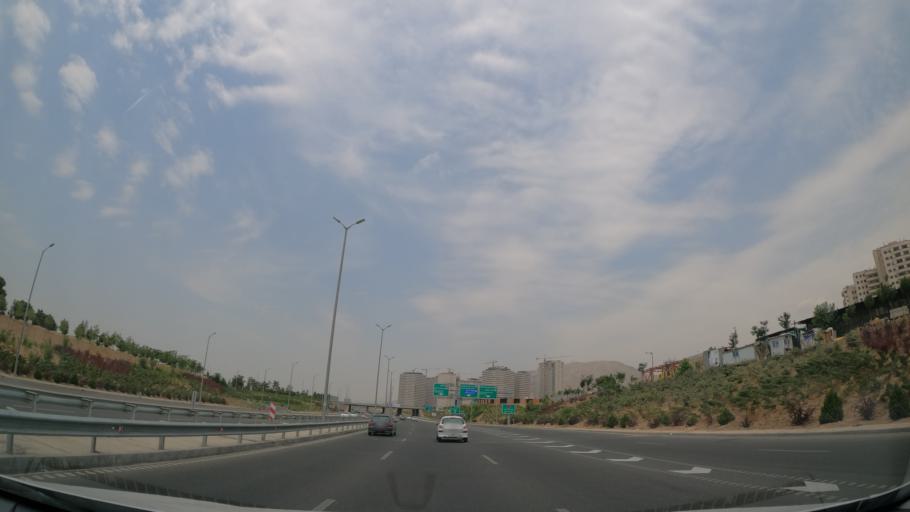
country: IR
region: Tehran
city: Shahr-e Qods
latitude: 35.7450
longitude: 51.1945
